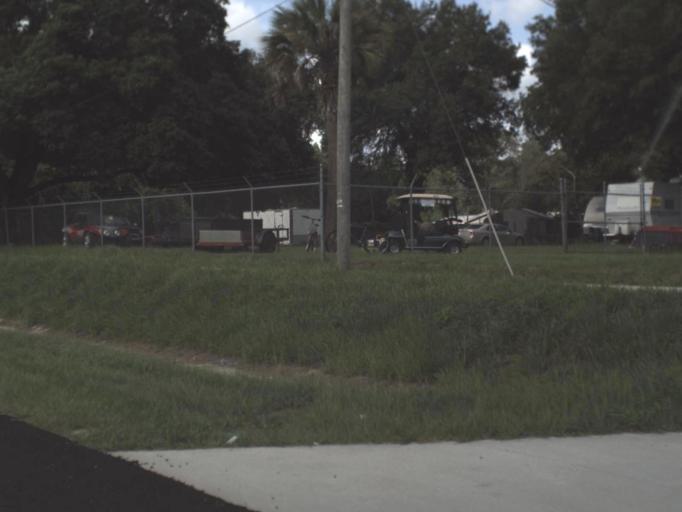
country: US
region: Florida
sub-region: Pasco County
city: Dade City North
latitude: 28.4257
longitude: -82.1910
